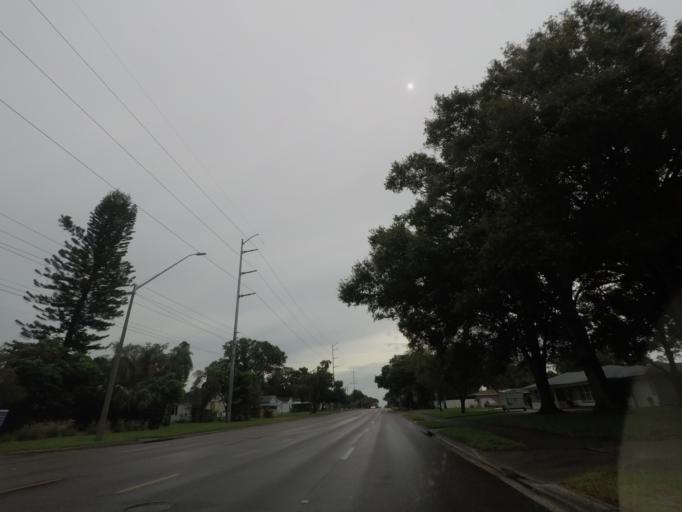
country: US
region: Florida
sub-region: Pinellas County
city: Kenneth City
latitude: 27.8064
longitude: -82.7070
